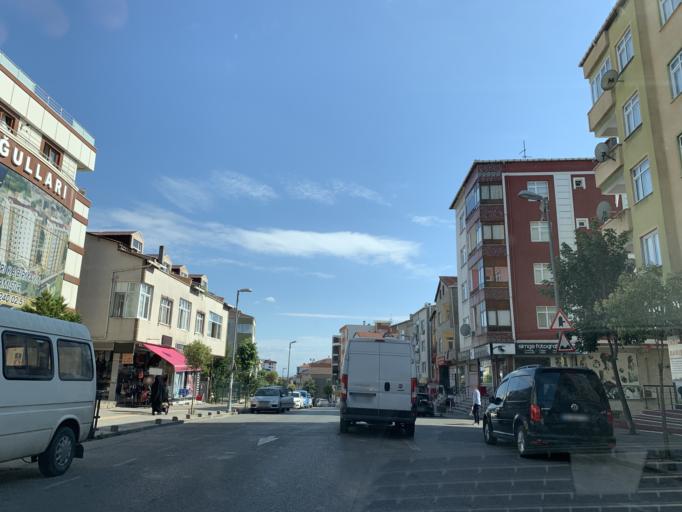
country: TR
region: Istanbul
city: Pendik
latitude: 40.8840
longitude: 29.2725
